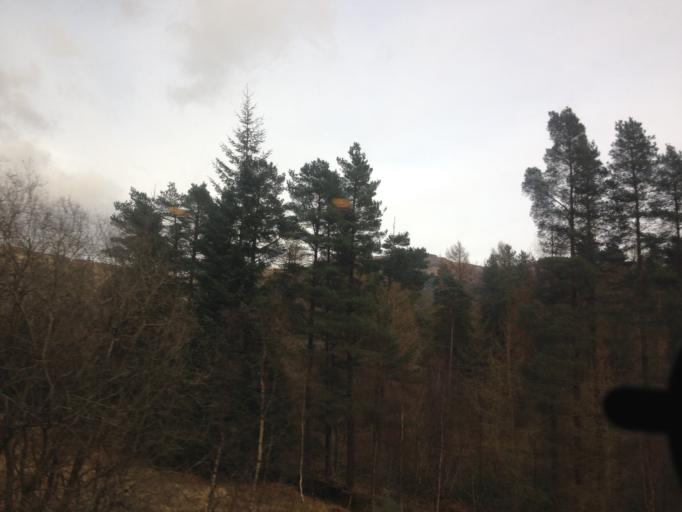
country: GB
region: Scotland
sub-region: Argyll and Bute
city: Garelochhead
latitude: 56.2113
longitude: -4.7031
